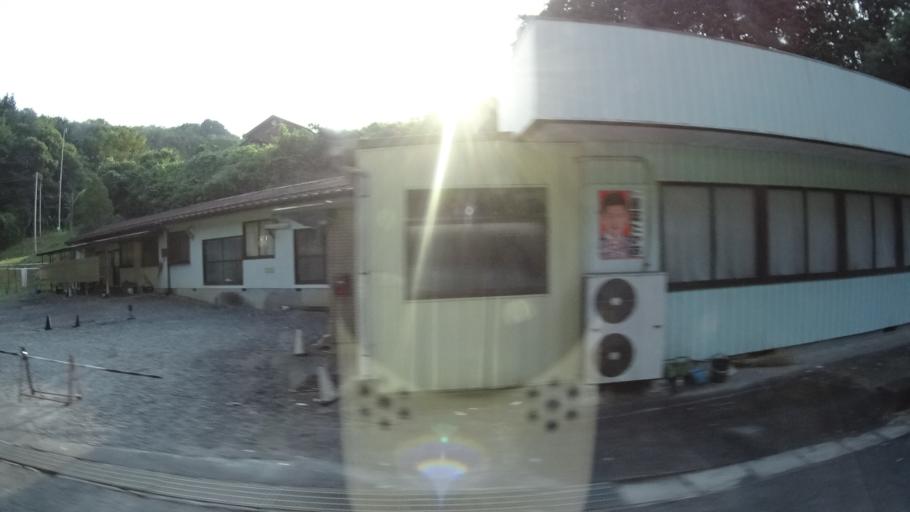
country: JP
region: Tochigi
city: Karasuyama
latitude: 36.6078
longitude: 140.1534
